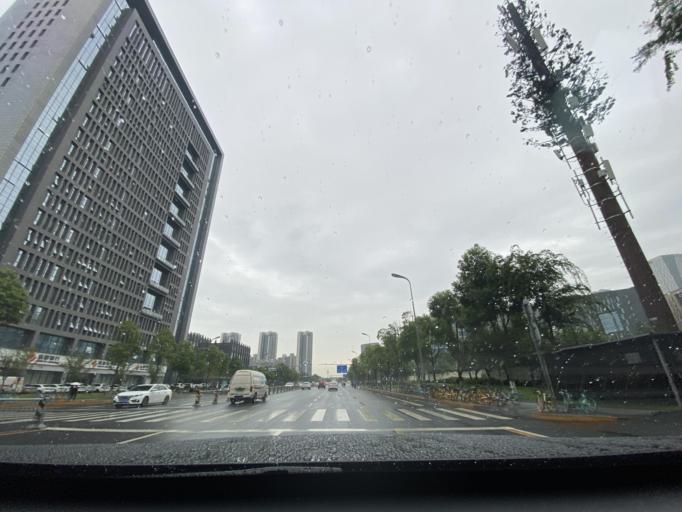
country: CN
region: Sichuan
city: Chengdu
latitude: 30.5447
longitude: 104.0633
